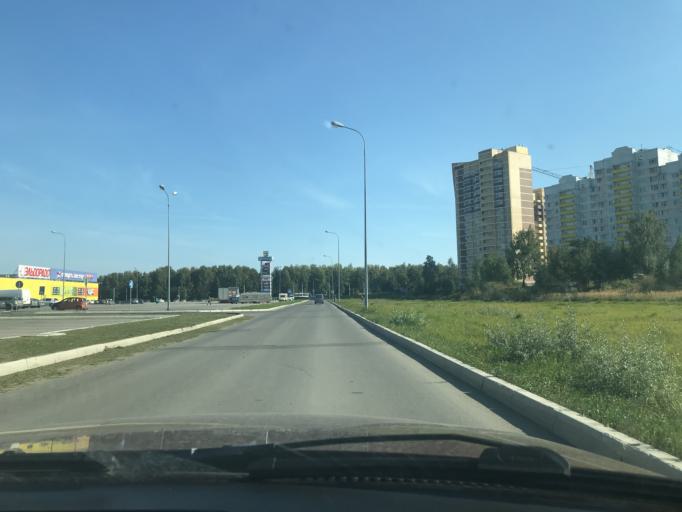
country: RU
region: Kaluga
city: Kaluga
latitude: 54.5855
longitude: 36.2476
